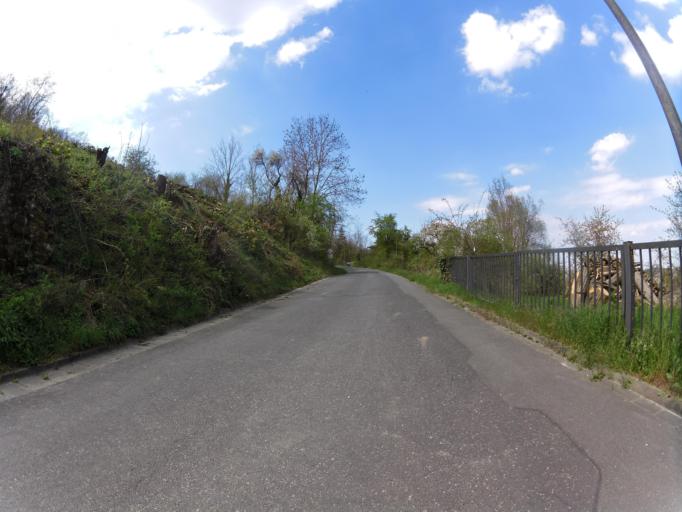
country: DE
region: Bavaria
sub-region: Regierungsbezirk Unterfranken
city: Sommerhausen
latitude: 49.6827
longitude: 10.0229
